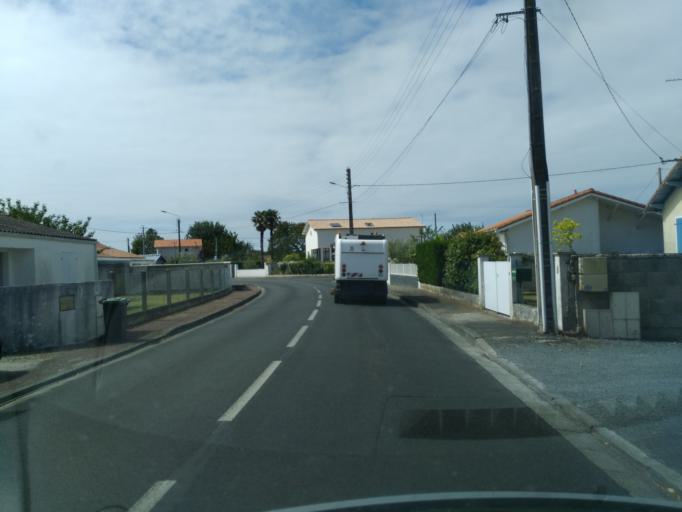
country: FR
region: Poitou-Charentes
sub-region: Departement de la Charente-Maritime
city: Saint-Palais-sur-Mer
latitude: 45.6551
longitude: -1.0783
